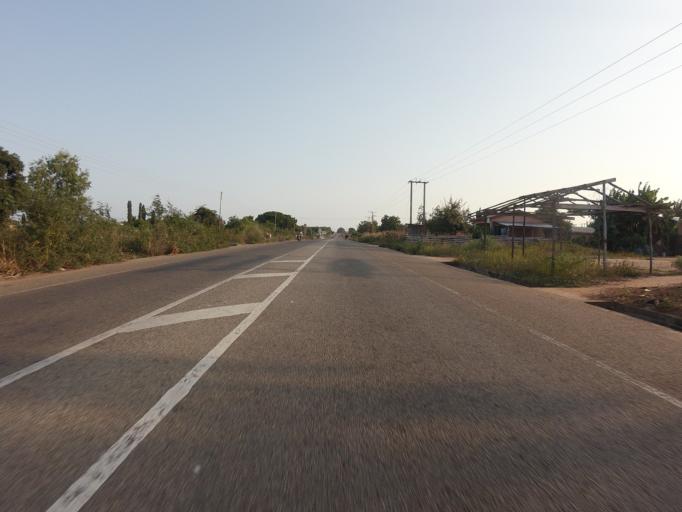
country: GH
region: Volta
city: Anloga
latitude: 6.0171
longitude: 0.5990
